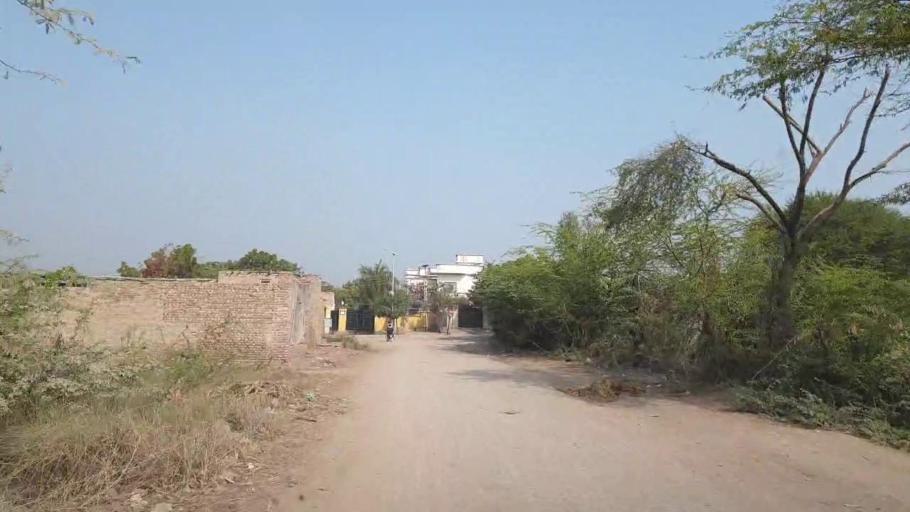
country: PK
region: Sindh
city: Mirpur Khas
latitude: 25.5426
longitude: 69.0230
